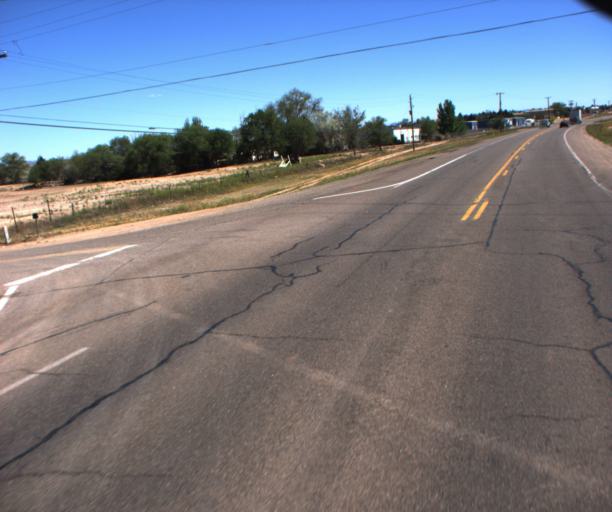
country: US
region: Arizona
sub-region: Yavapai County
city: Chino Valley
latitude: 34.8048
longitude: -112.4503
